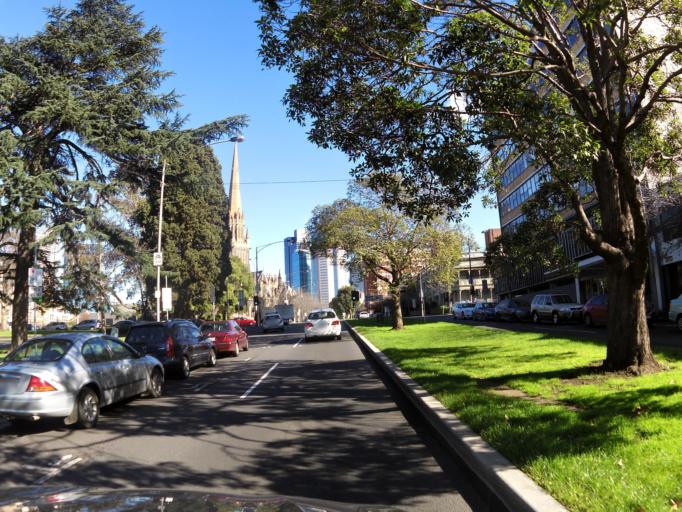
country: AU
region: Victoria
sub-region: Yarra
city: Collingwood
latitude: -37.8100
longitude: 144.9791
